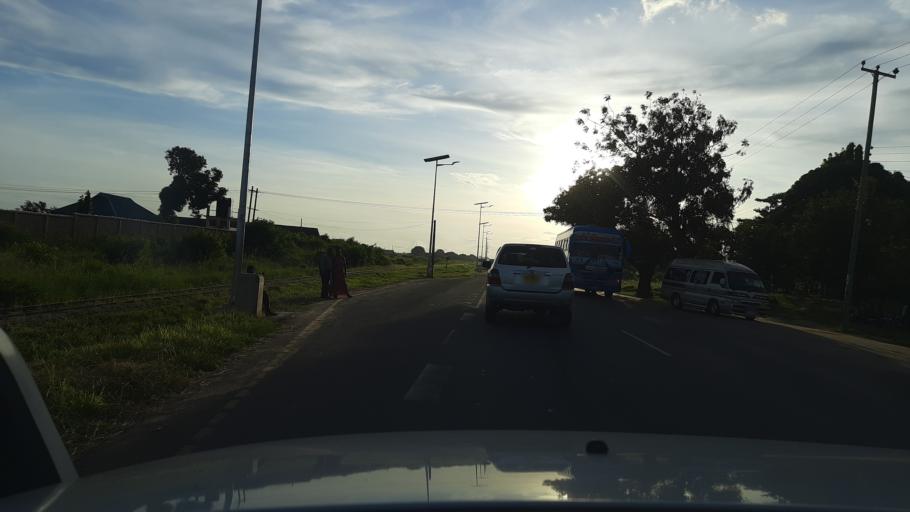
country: TZ
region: Tanga
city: Tanga
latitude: -5.0845
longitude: 39.0778
